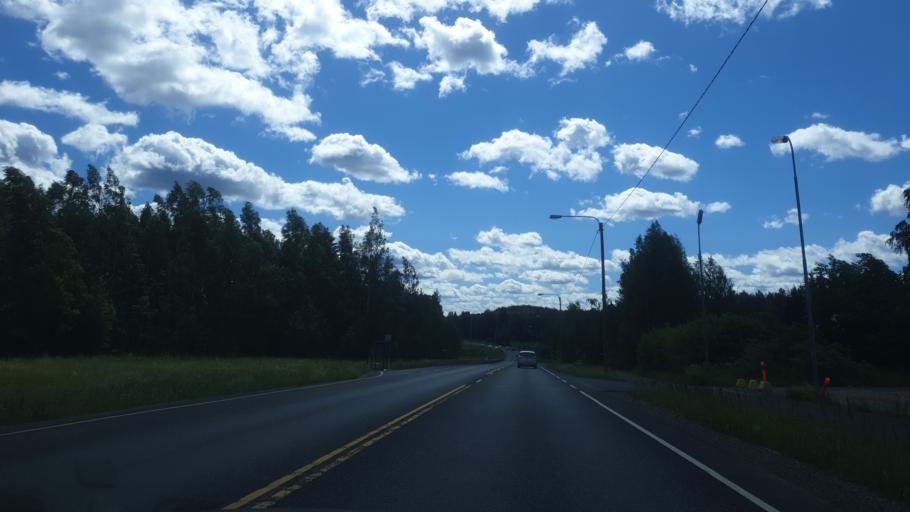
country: FI
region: Northern Savo
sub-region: Varkaus
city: Leppaevirta
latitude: 62.6411
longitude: 27.6089
